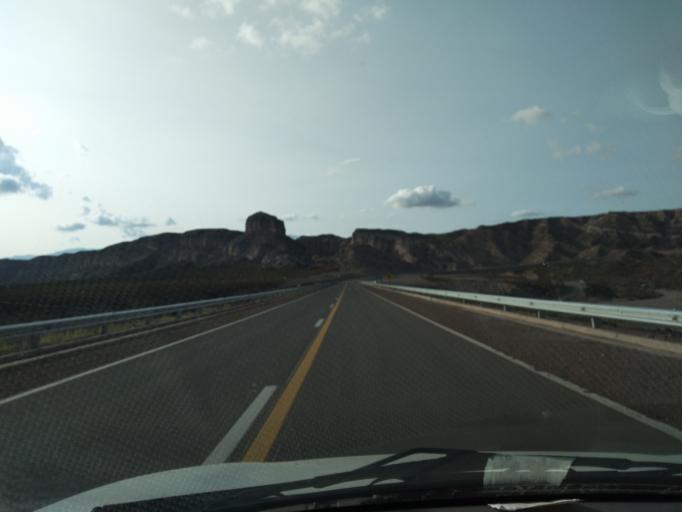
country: AR
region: Mendoza
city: San Rafael
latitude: -34.6405
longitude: -69.1788
